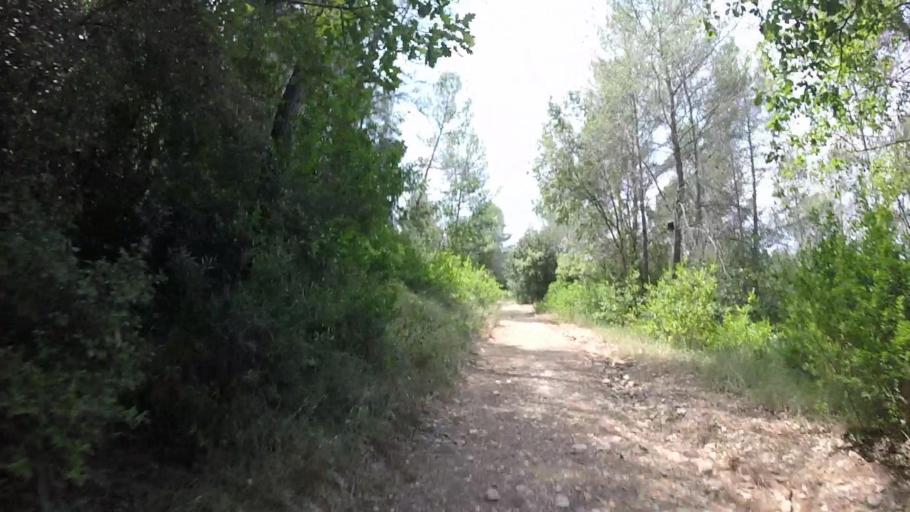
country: FR
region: Provence-Alpes-Cote d'Azur
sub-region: Departement des Alpes-Maritimes
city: Valbonne
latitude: 43.6307
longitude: 7.0403
